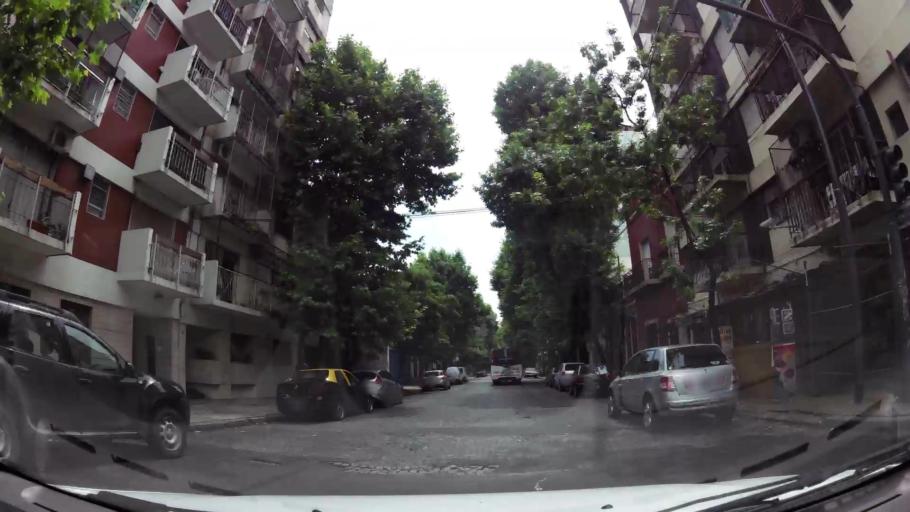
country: AR
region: Buenos Aires F.D.
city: Retiro
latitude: -34.6005
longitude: -58.4163
